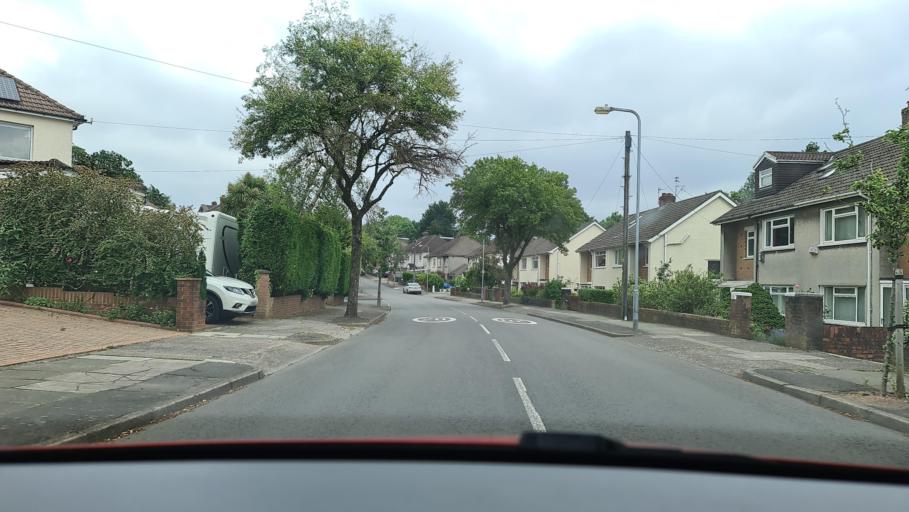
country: GB
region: Wales
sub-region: Cardiff
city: Cardiff
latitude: 51.5026
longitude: -3.1699
